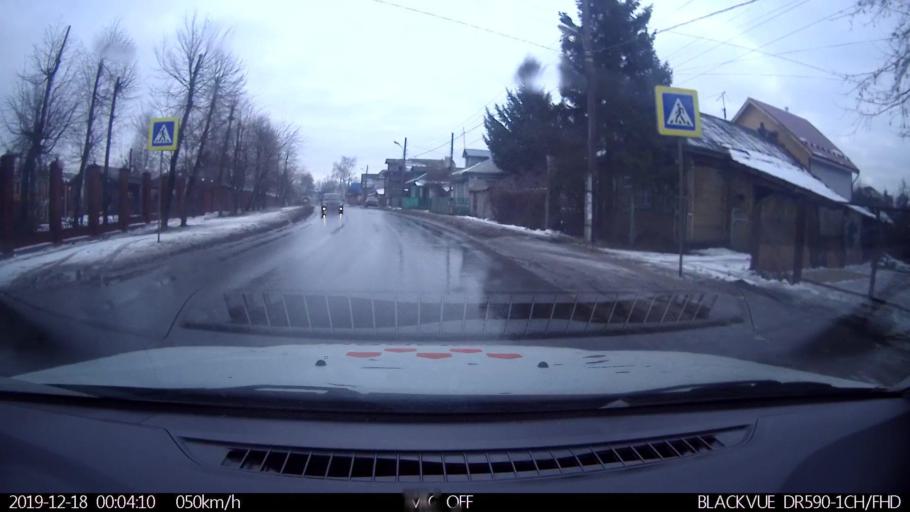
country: RU
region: Nizjnij Novgorod
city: Neklyudovo
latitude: 56.3669
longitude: 43.8441
